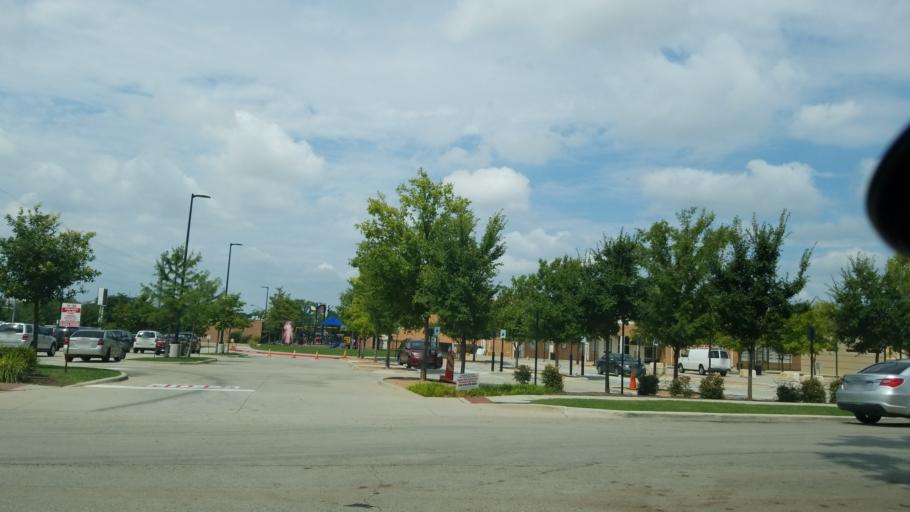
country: US
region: Texas
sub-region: Dallas County
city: Garland
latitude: 32.9116
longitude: -96.6465
